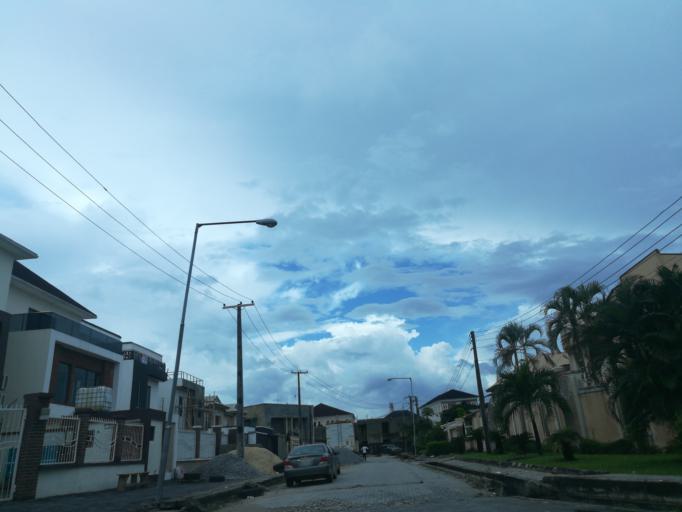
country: NG
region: Lagos
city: Ikoyi
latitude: 6.4427
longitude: 3.4731
